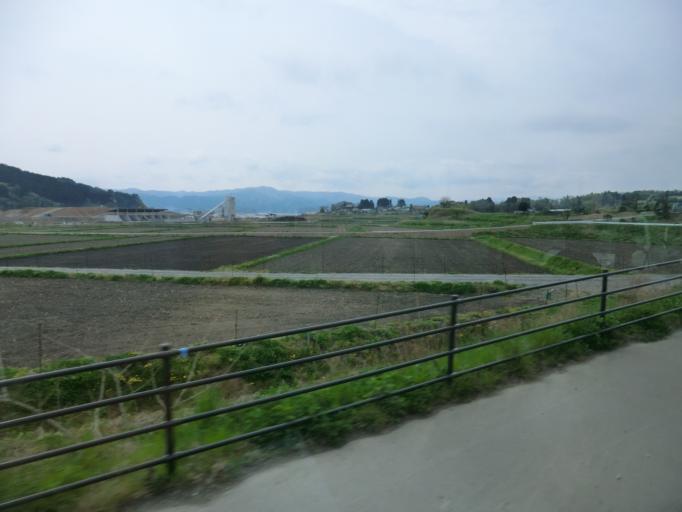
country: JP
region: Iwate
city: Ofunato
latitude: 38.9978
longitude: 141.6914
